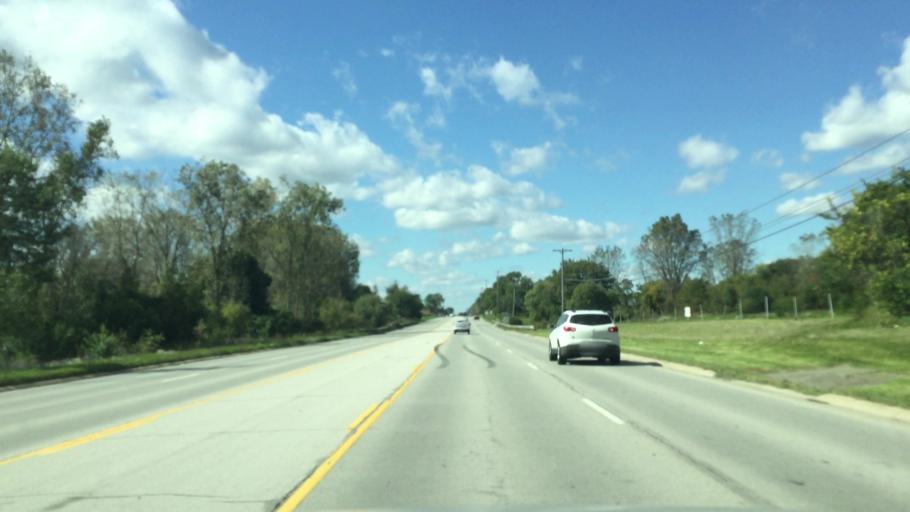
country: US
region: Michigan
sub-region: Genesee County
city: Flint
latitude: 42.9439
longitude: -83.7419
